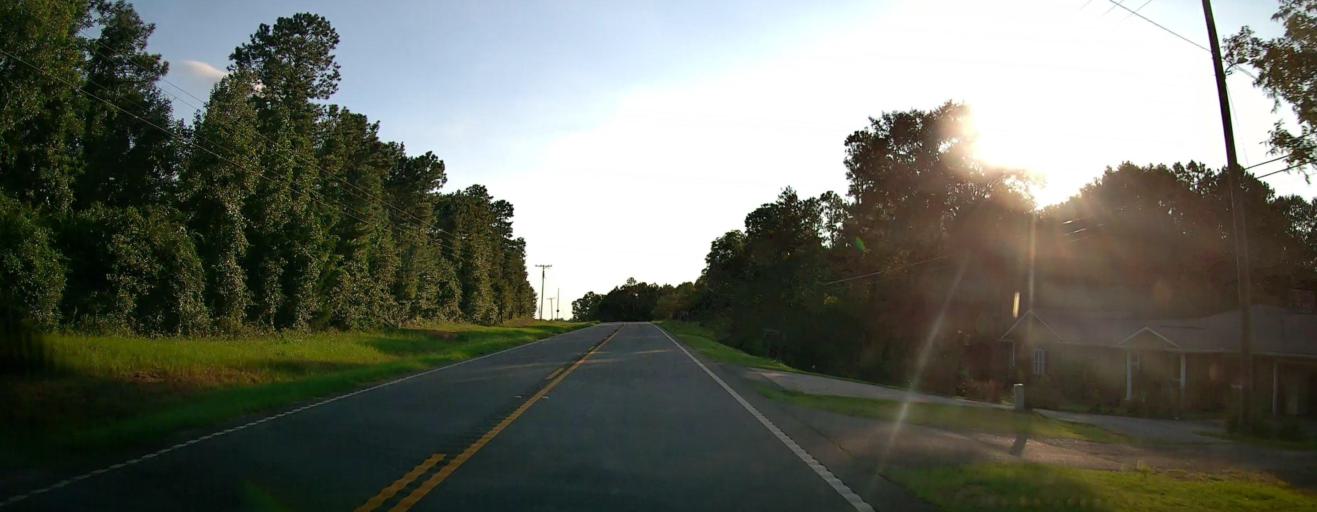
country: US
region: Georgia
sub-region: Crawford County
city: Roberta
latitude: 32.7089
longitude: -84.0294
